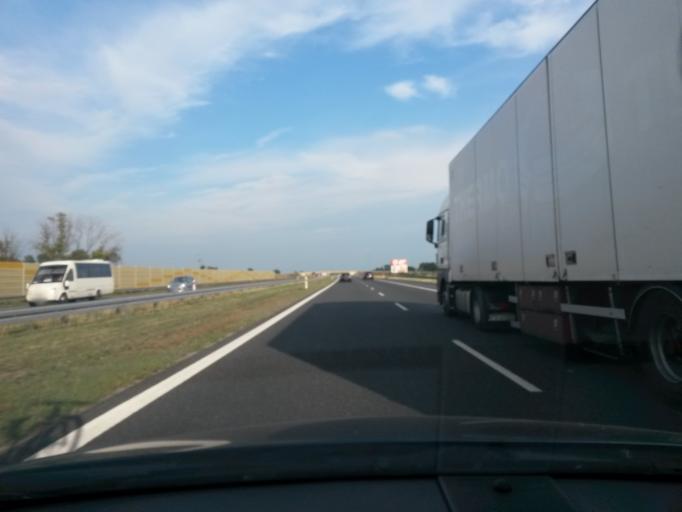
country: PL
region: Lodz Voivodeship
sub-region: Powiat poddebicki
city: Dalikow
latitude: 51.9697
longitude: 19.0960
